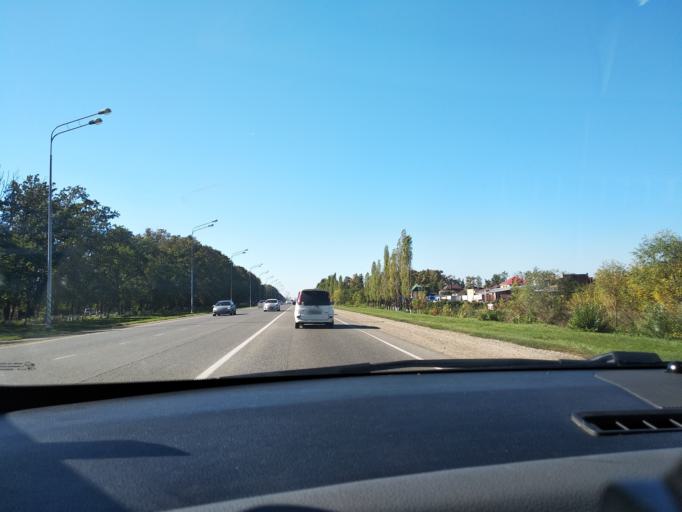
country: RU
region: Krasnodarskiy
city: Novotitarovskaya
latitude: 45.1485
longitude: 39.0550
